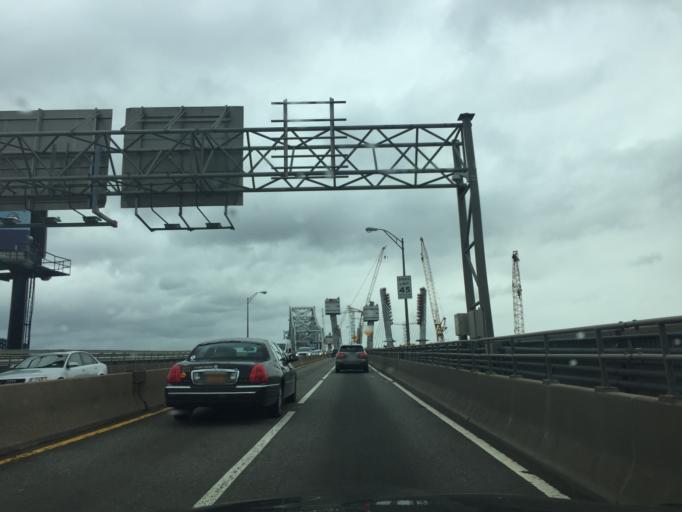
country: US
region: New Jersey
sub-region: Union County
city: Elizabeth
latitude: 40.6386
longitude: -74.2019
